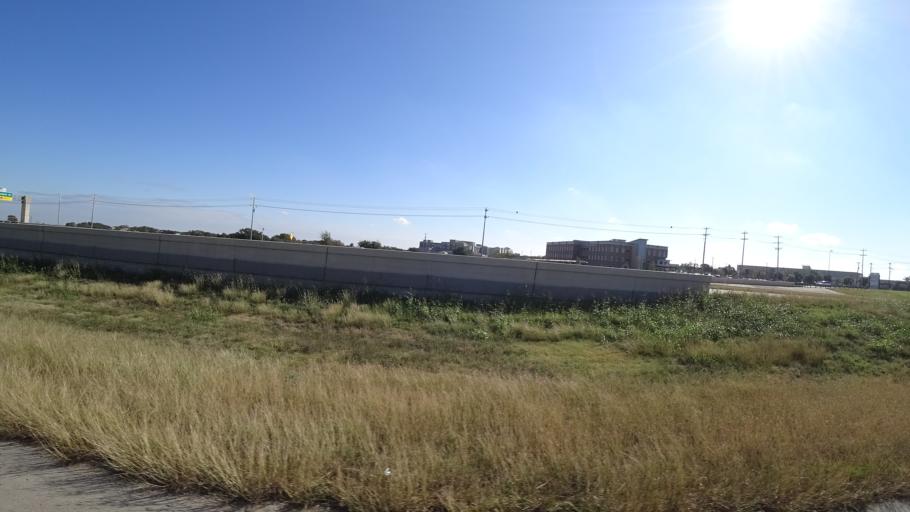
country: US
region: Texas
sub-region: Williamson County
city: Cedar Park
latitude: 30.5337
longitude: -97.8174
